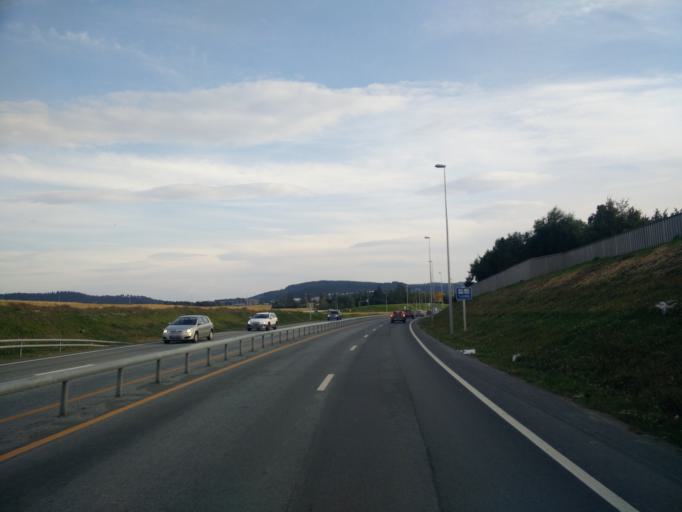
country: NO
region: Sor-Trondelag
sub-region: Trondheim
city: Trondheim
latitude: 63.4299
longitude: 10.4759
